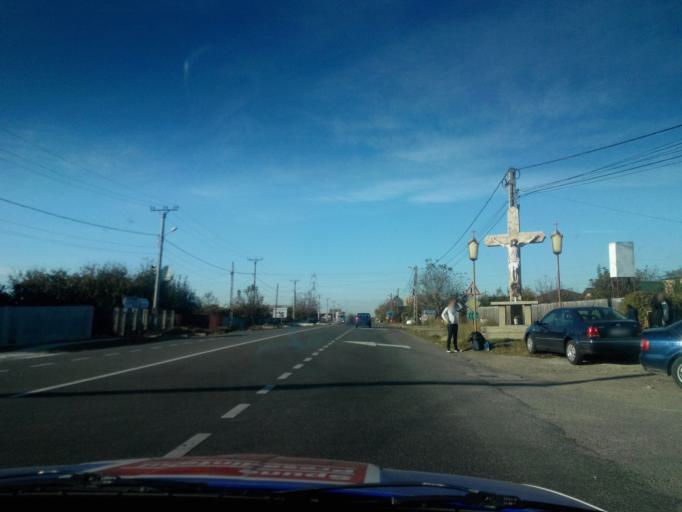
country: RO
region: Bacau
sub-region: Comuna Saucesti
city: Saucesti
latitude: 46.6067
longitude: 26.9281
